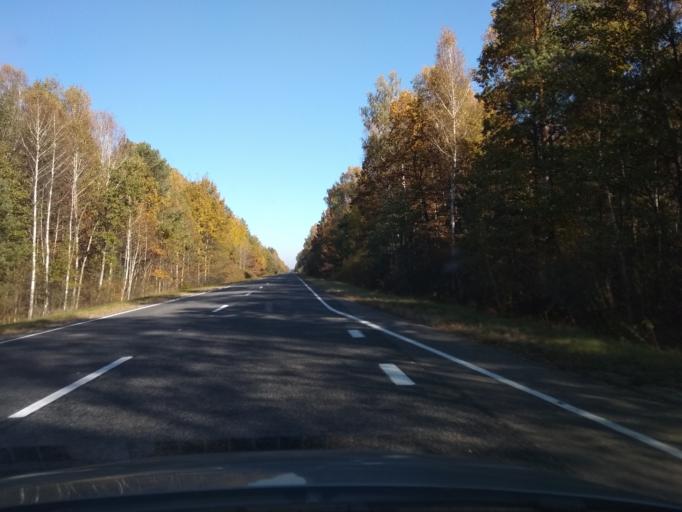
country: BY
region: Brest
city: Malaryta
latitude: 51.9321
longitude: 24.1690
